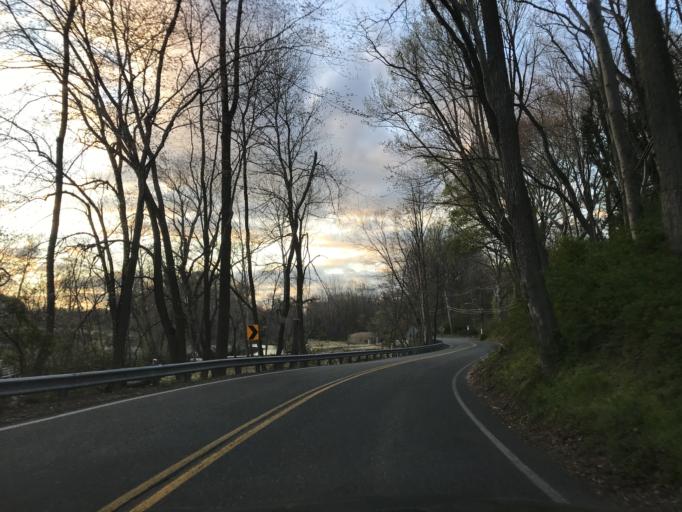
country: US
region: Maryland
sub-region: Harford County
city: Bel Air South
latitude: 39.5252
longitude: -76.3152
